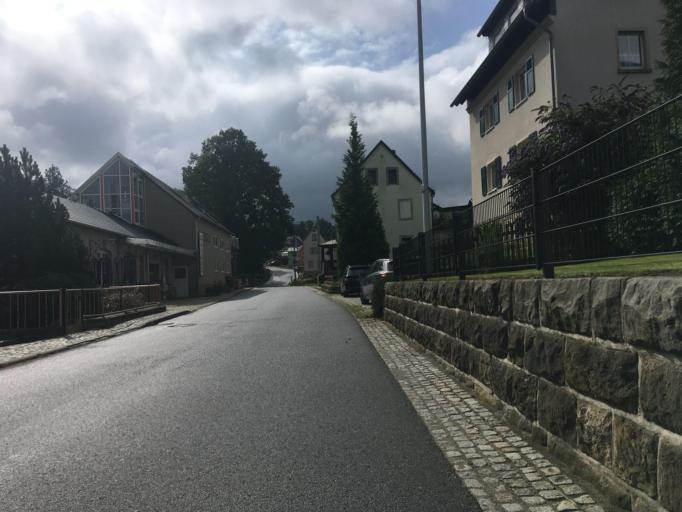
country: DE
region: Saxony
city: Bad Schandau
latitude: 50.8911
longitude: 14.1948
